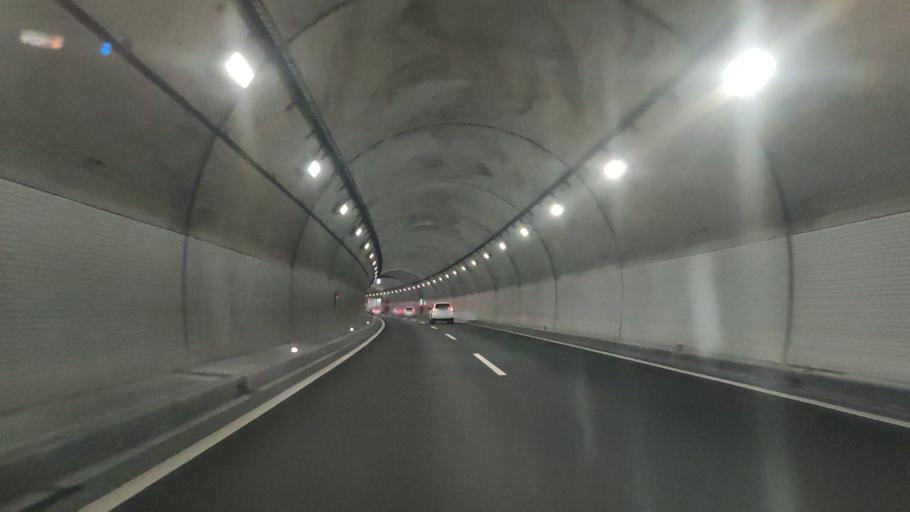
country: JP
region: Fukuoka
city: Kanda
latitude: 33.8031
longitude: 130.9453
